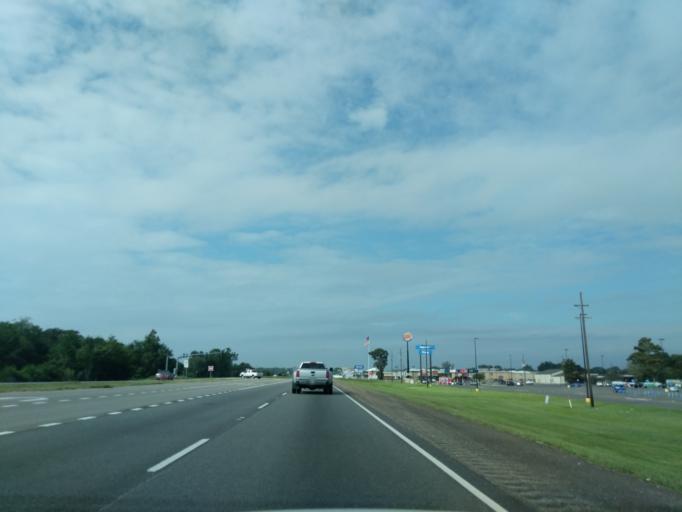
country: US
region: Louisiana
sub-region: Saint Mary Parish
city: Bayou Vista
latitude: 29.6820
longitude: -91.2658
